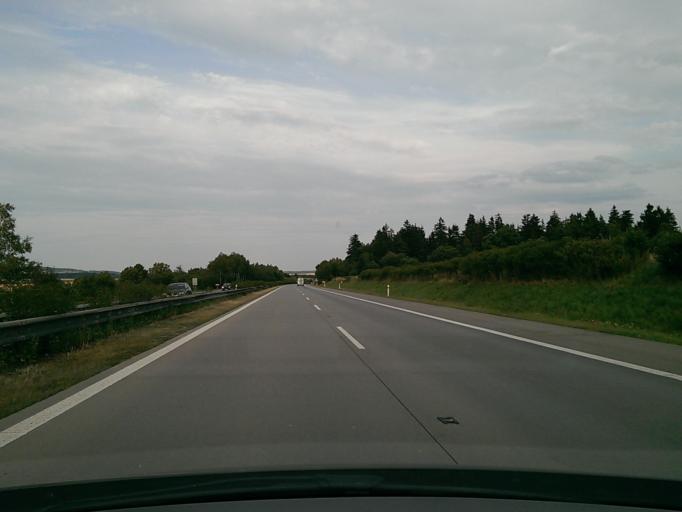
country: CZ
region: Vysocina
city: Merin
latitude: 49.4050
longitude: 15.8289
